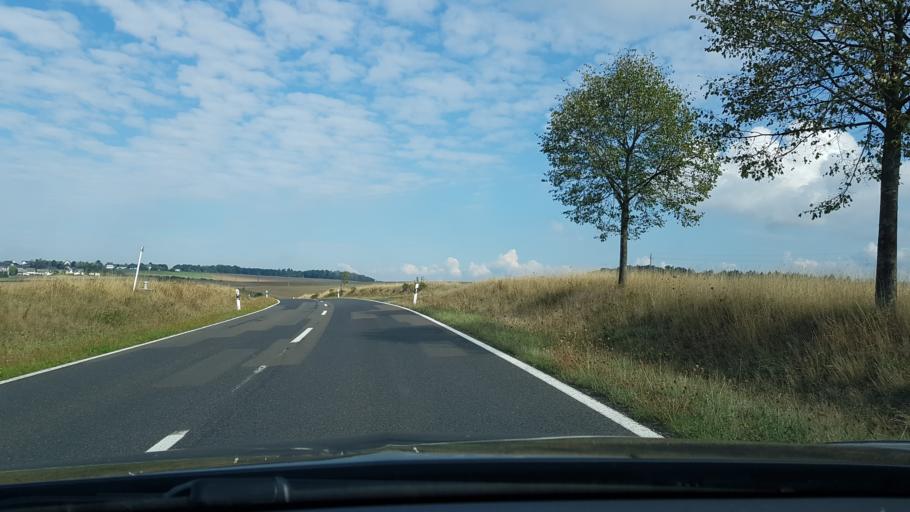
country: DE
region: Rheinland-Pfalz
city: Beulich
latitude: 50.1803
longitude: 7.4533
